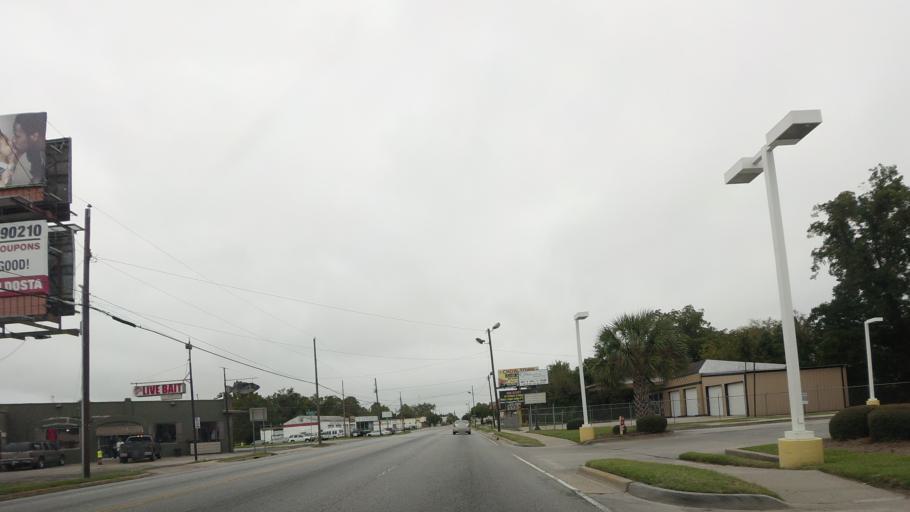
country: US
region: Georgia
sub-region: Lowndes County
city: Valdosta
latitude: 30.8225
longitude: -83.2744
